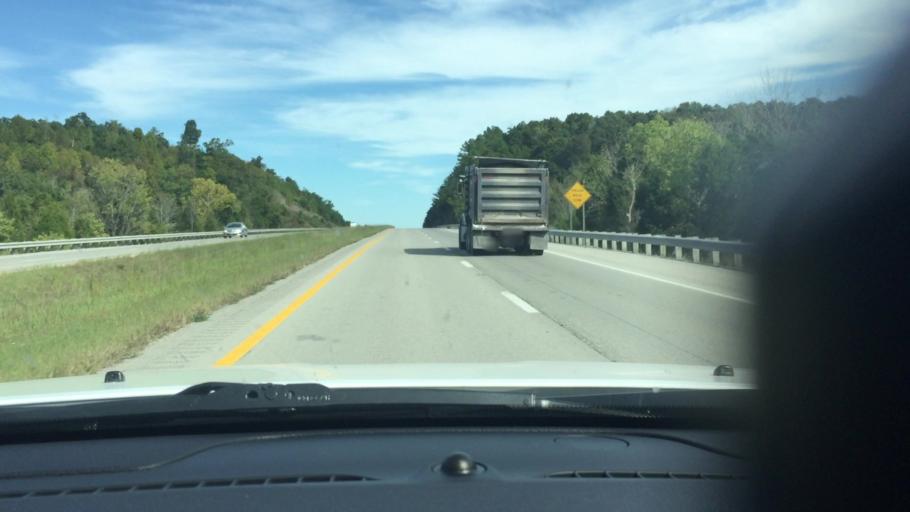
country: US
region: Kentucky
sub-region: Caldwell County
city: Princeton
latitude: 37.1400
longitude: -87.8375
